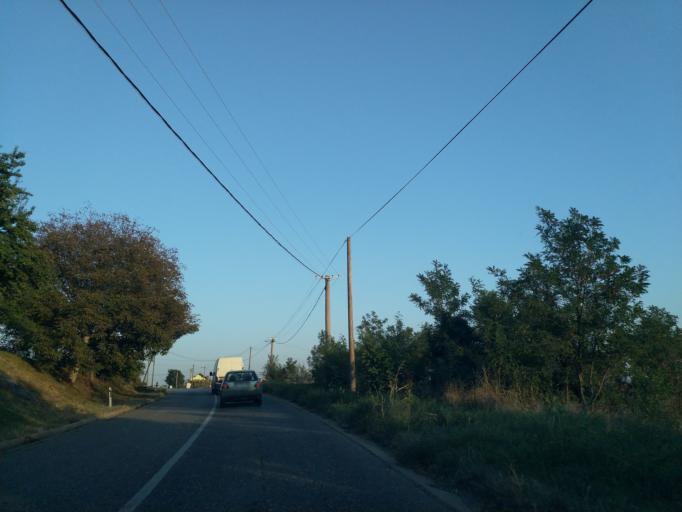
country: RS
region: Central Serbia
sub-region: Rasinski Okrug
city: Trstenik
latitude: 43.6316
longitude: 21.0370
